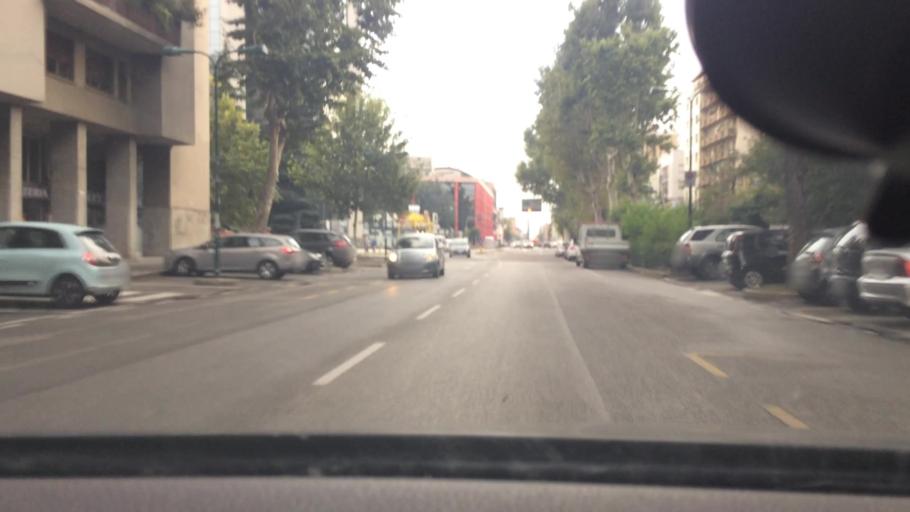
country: IT
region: Lombardy
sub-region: Citta metropolitana di Milano
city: Sesto San Giovanni
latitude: 45.5281
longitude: 9.2293
